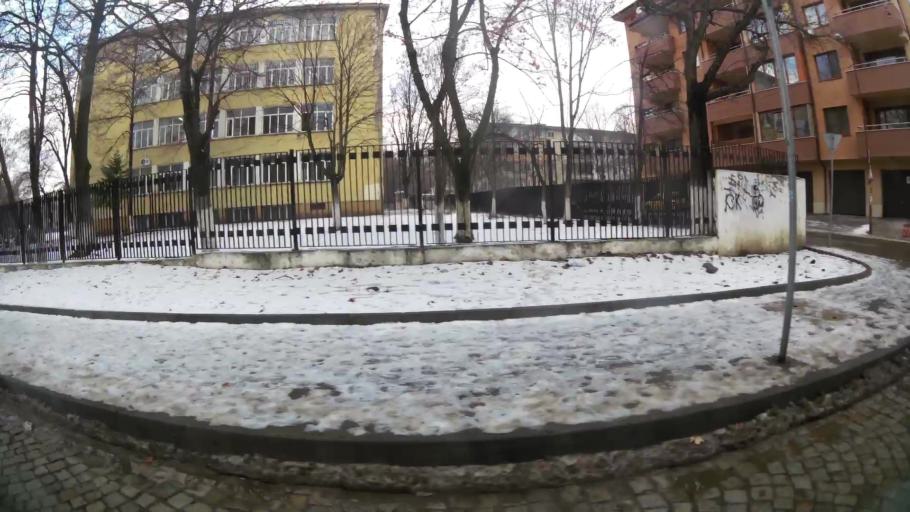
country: BG
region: Sofia-Capital
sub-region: Stolichna Obshtina
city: Sofia
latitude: 42.7058
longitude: 23.2782
